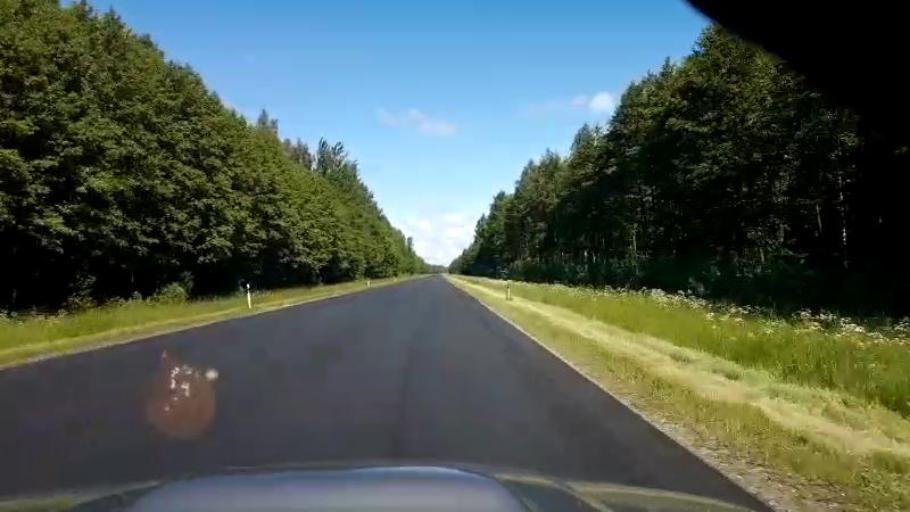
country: LV
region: Salacgrivas
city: Ainazi
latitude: 57.9551
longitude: 24.4399
